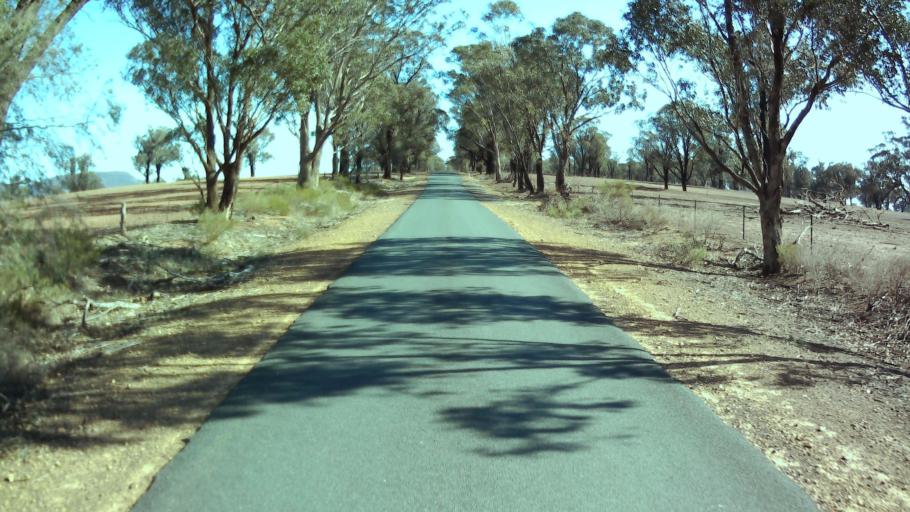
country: AU
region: New South Wales
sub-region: Weddin
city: Grenfell
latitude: -33.7890
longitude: 147.9578
